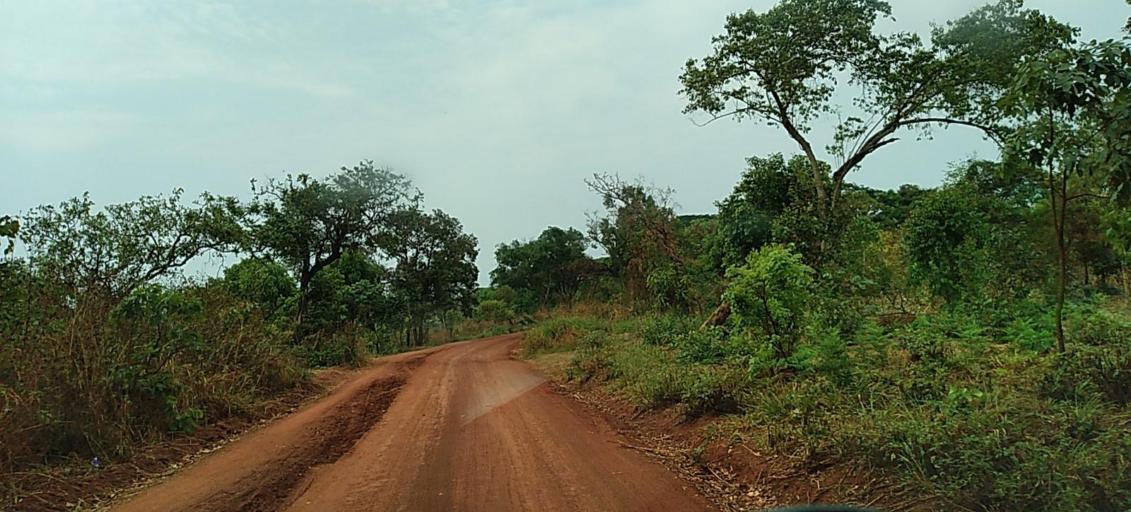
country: ZM
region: North-Western
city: Solwezi
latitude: -12.2493
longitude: 26.5129
